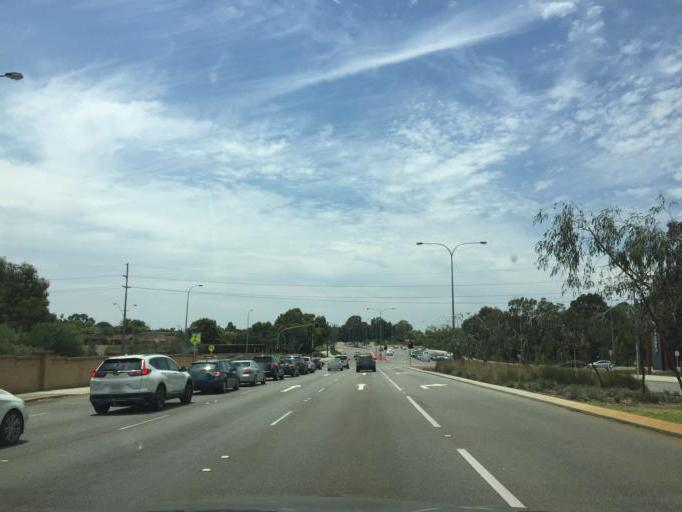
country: AU
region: Western Australia
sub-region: Melville
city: Winthrop
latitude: -32.0650
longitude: 115.8411
